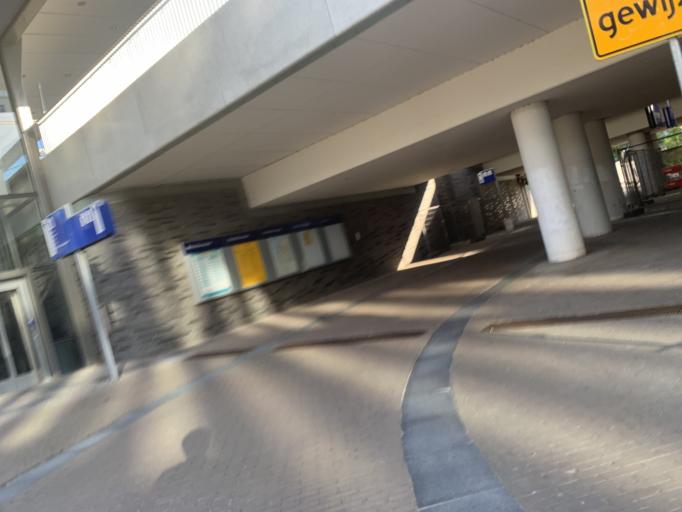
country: NL
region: Groningen
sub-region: Gemeente Groningen
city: Oosterpark
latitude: 53.2049
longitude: 6.5859
